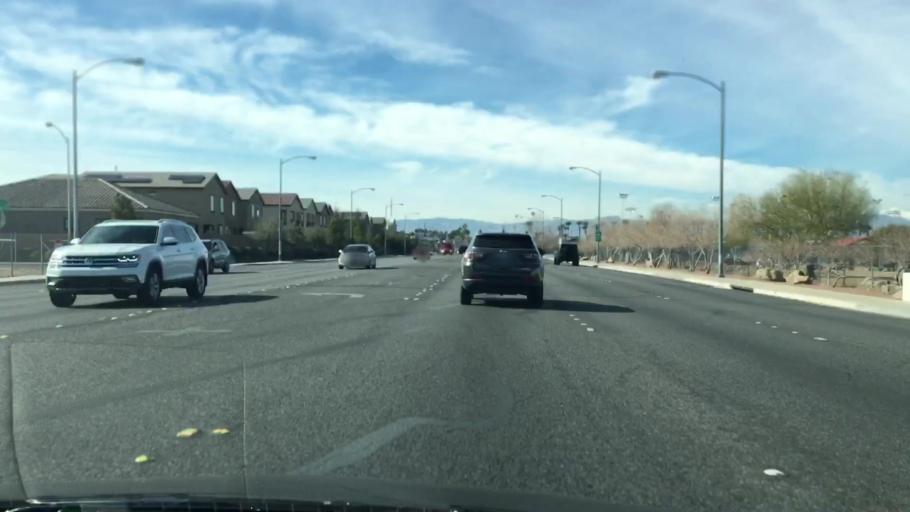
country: US
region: Nevada
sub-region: Clark County
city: Whitney
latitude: 36.0570
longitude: -115.1133
